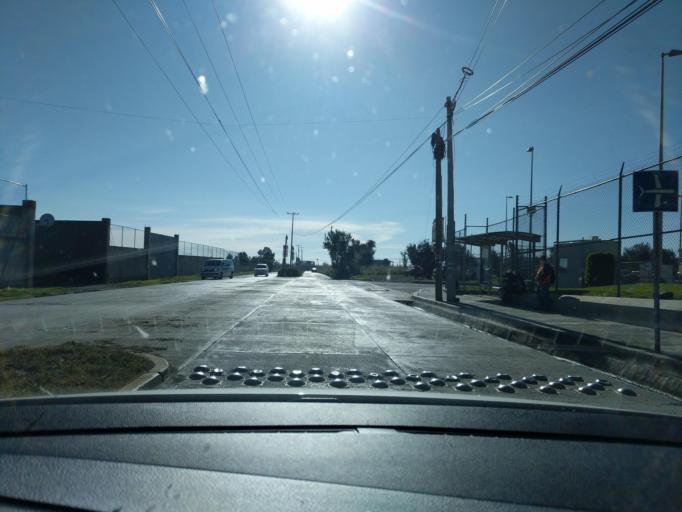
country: MX
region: Puebla
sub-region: Huejotzingo
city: Los Encinos
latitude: 19.1722
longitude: -98.3793
